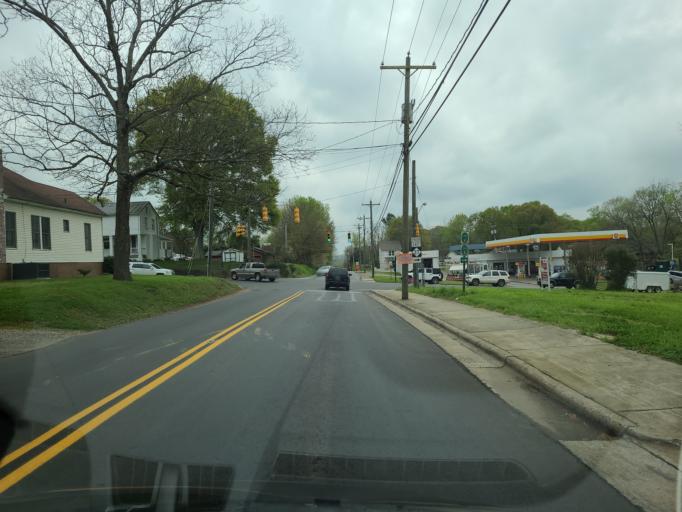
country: US
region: North Carolina
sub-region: Lincoln County
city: Lincolnton
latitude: 35.4703
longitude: -81.2619
